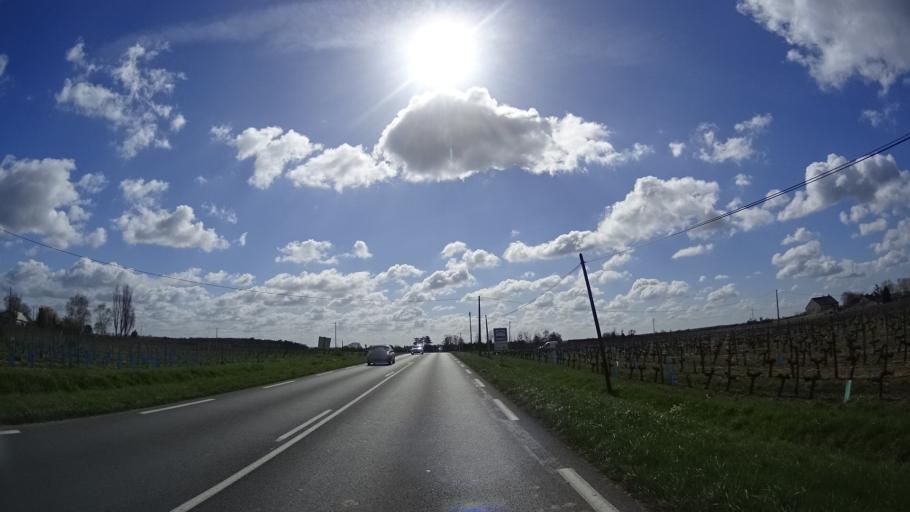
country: FR
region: Pays de la Loire
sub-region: Departement de Maine-et-Loire
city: Brissac-Quince
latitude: 47.3371
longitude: -0.4294
